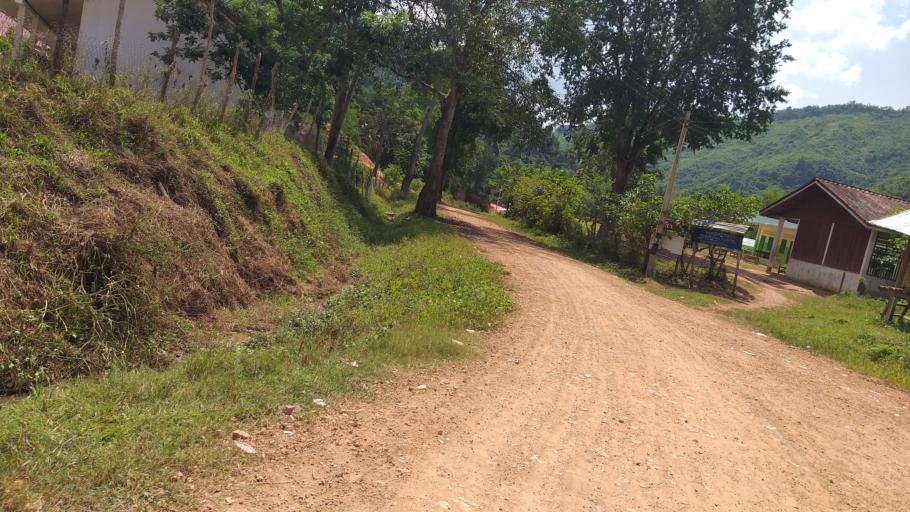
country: LA
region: Phongsali
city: Khoa
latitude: 21.3223
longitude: 102.5688
